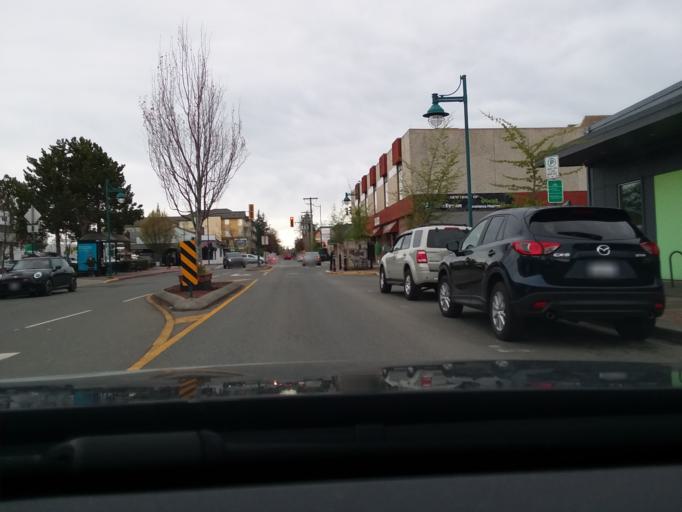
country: CA
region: British Columbia
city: North Saanich
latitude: 48.6482
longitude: -123.4003
